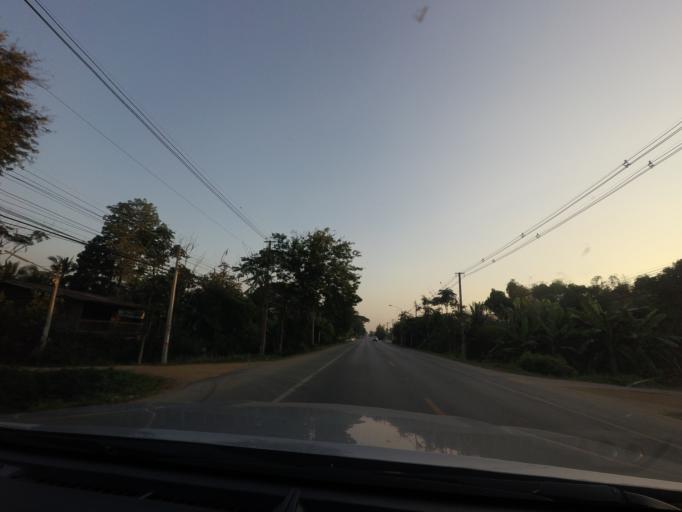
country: TH
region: Sukhothai
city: Si Samrong
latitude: 17.1269
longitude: 99.8506
